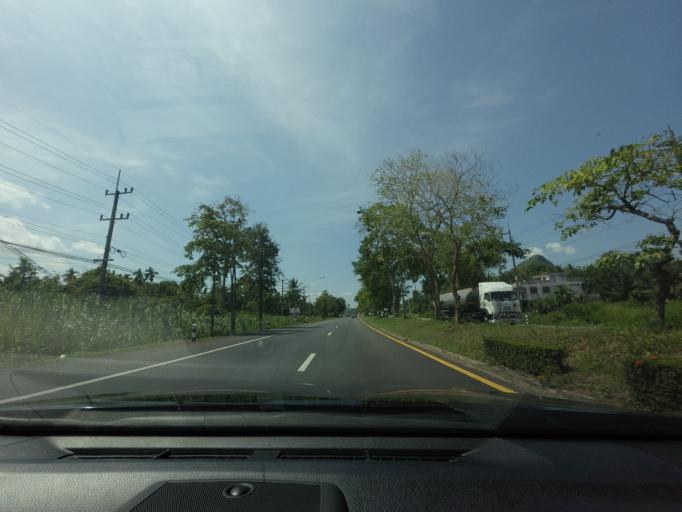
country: TH
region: Chumphon
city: Chumphon
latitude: 10.5552
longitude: 99.1166
